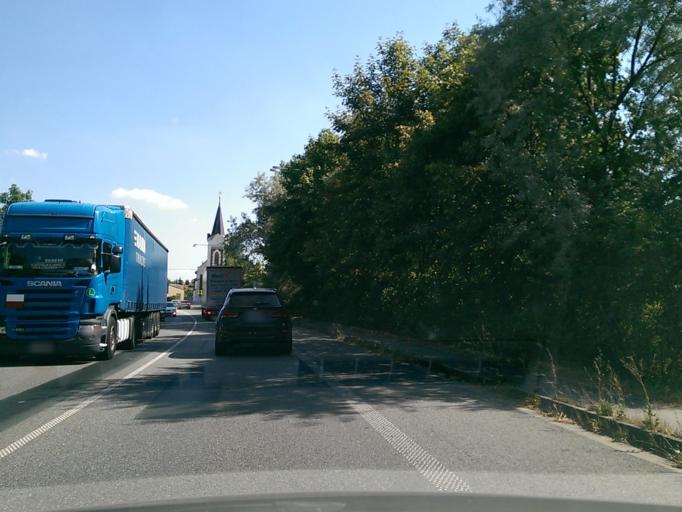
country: CZ
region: South Moravian
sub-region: Okres Breclav
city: Mikulov
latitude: 48.8028
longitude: 16.6273
